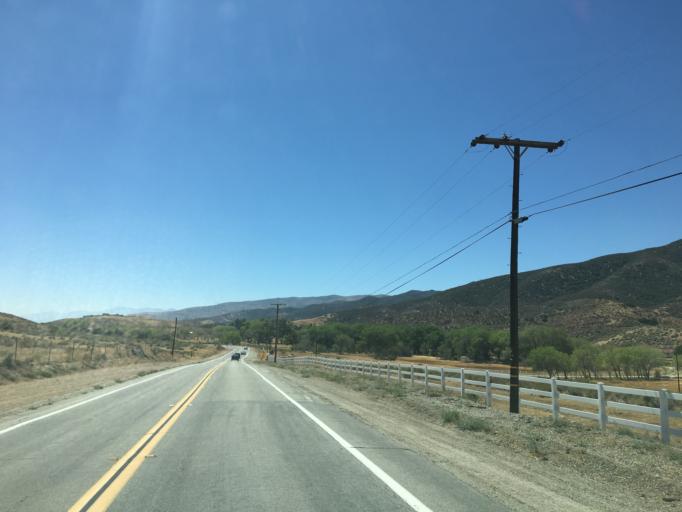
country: US
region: California
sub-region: Los Angeles County
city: Leona Valley
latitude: 34.6327
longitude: -118.3357
